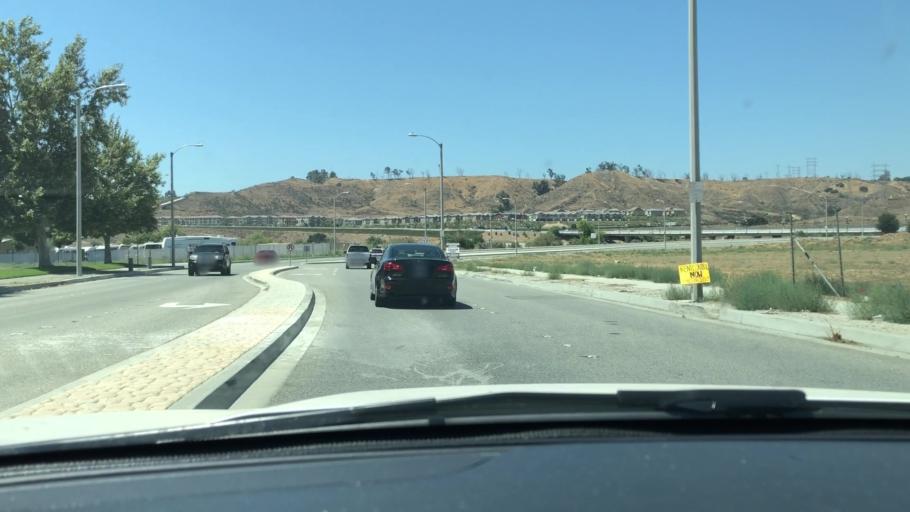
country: US
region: California
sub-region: Los Angeles County
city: Santa Clarita
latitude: 34.4216
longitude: -118.5047
